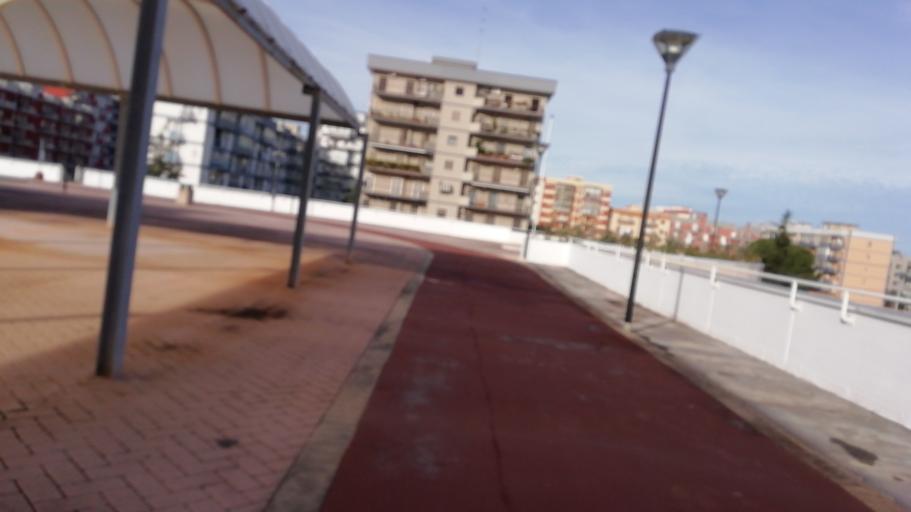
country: IT
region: Apulia
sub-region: Provincia di Bari
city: Triggiano
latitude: 41.1058
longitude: 16.9117
